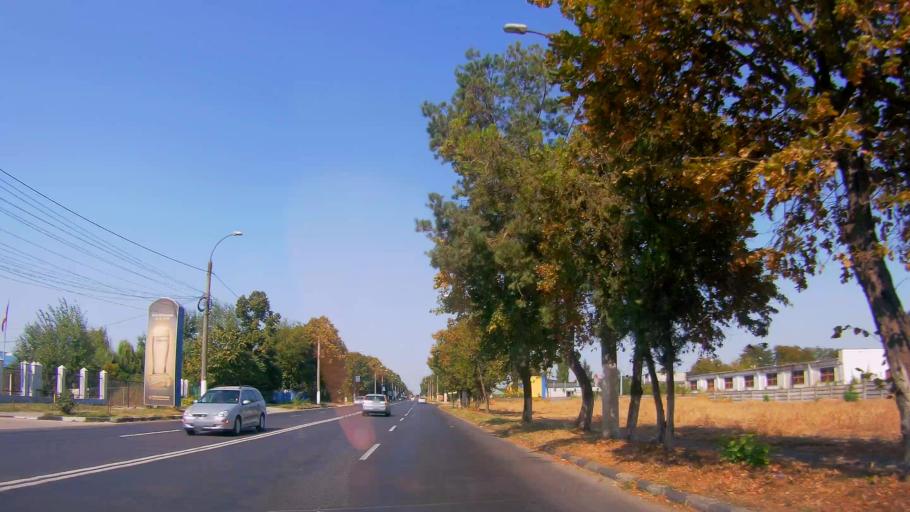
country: RO
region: Giurgiu
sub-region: Comuna Fratesti
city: Remus
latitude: 43.9207
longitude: 25.9733
